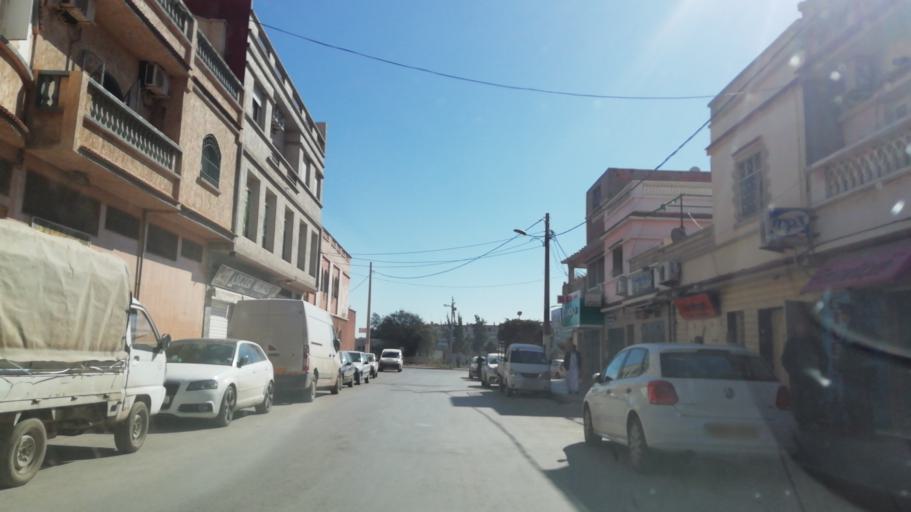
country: DZ
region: Oran
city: Oran
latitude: 35.6929
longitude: -0.6134
